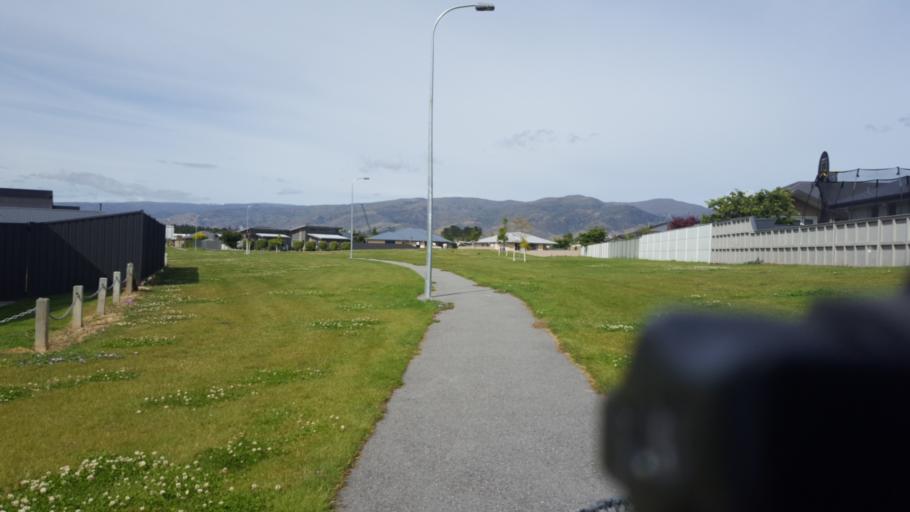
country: NZ
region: Otago
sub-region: Queenstown-Lakes District
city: Wanaka
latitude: -45.0459
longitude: 169.1889
